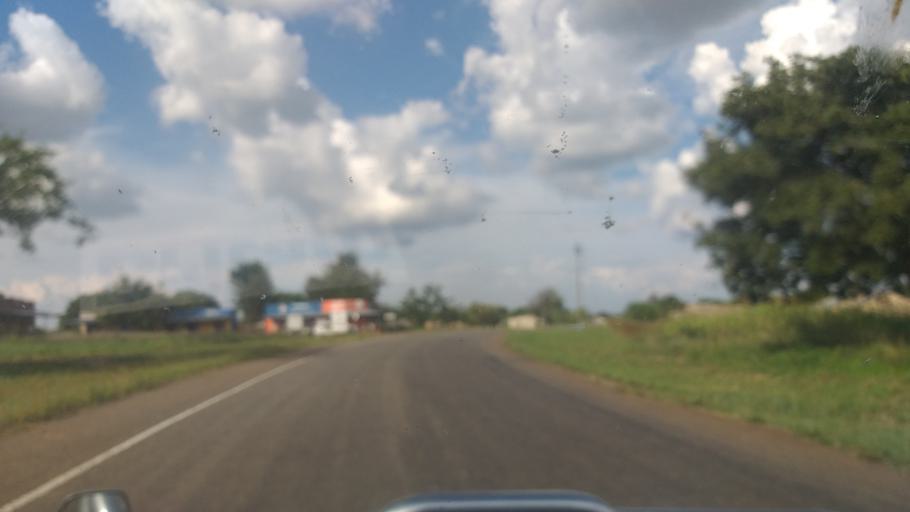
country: UG
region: Northern Region
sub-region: Nebbi District
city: Nebbi
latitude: 2.5616
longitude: 31.1011
